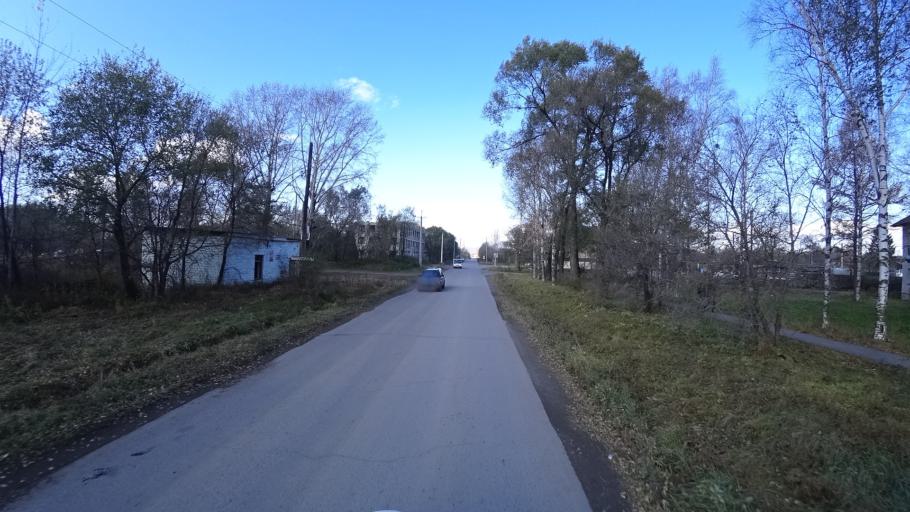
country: RU
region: Khabarovsk Krai
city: Amursk
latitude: 50.0948
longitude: 136.4995
